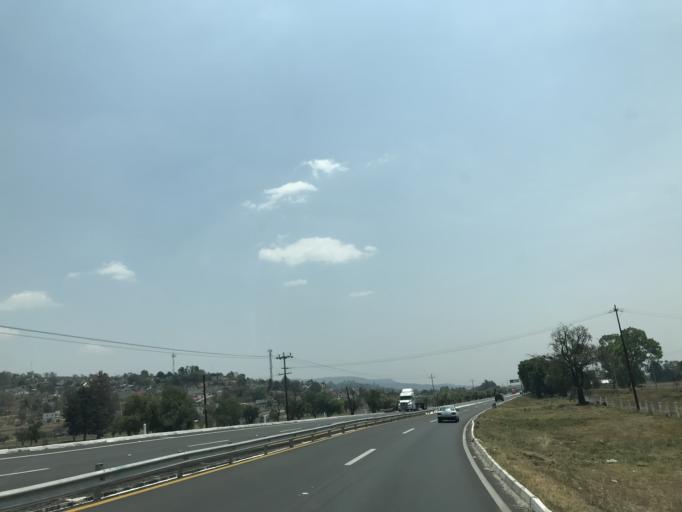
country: MX
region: Tlaxcala
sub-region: Ixtacuixtla de Mariano Matamoros
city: Santa Justina Ecatepec
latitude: 19.3293
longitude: -98.3551
